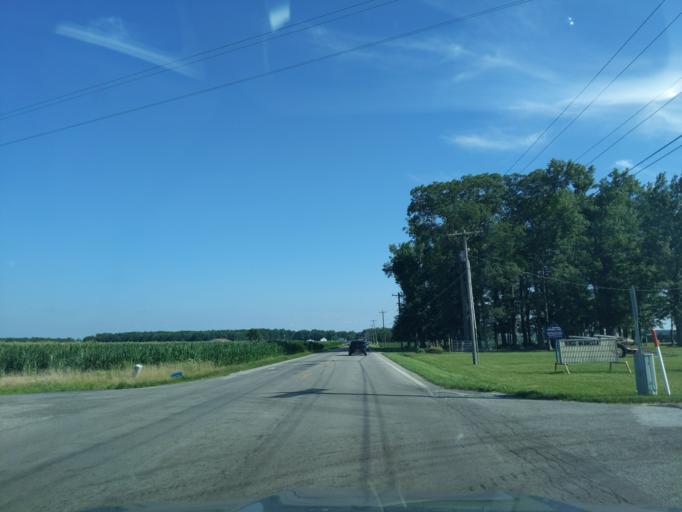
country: US
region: Indiana
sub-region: Ripley County
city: Osgood
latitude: 39.1622
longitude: -85.3078
